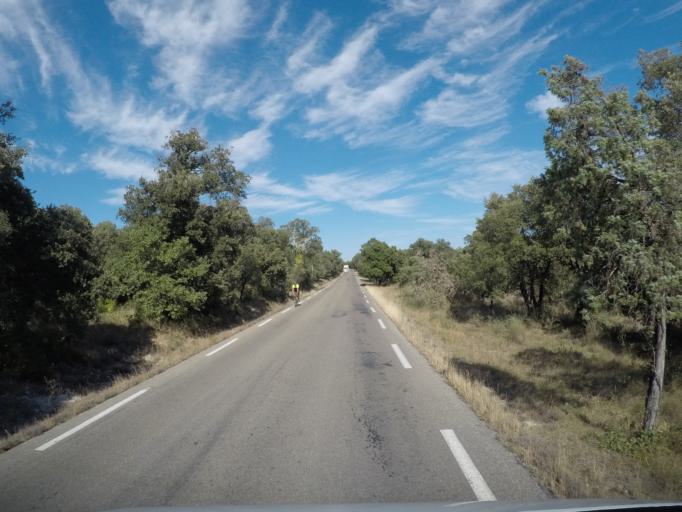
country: FR
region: Languedoc-Roussillon
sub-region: Departement du Gard
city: Anduze
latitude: 44.0004
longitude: 3.9772
